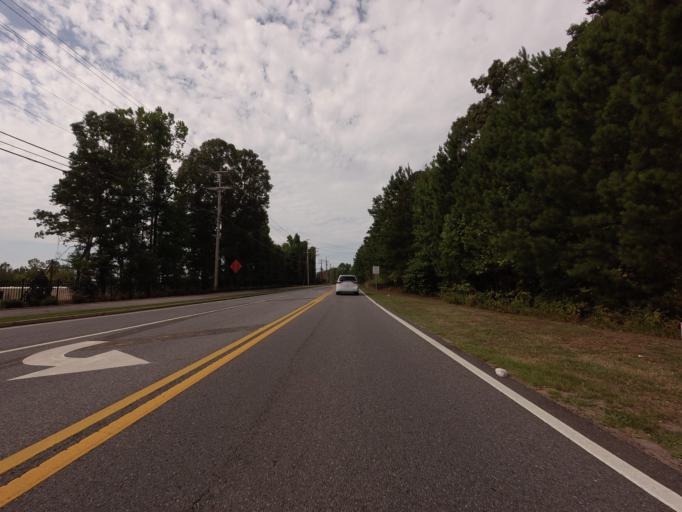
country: US
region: Georgia
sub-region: Gwinnett County
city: Duluth
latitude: 34.0559
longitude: -84.1322
